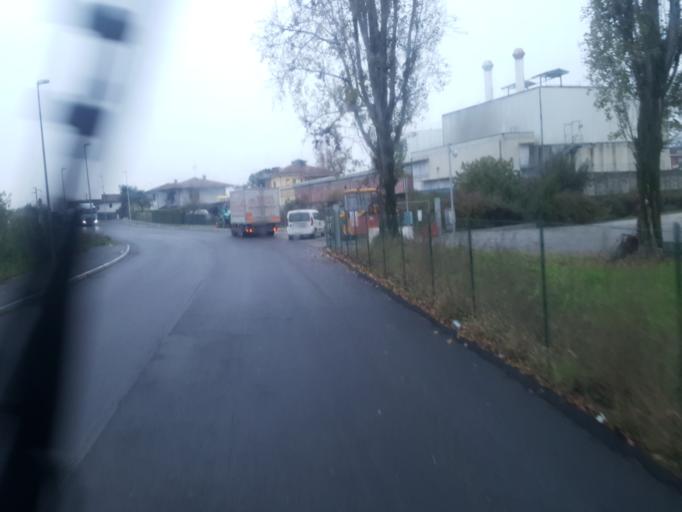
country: IT
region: Piedmont
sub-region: Provincia di Cuneo
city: Saluzzo
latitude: 44.6409
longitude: 7.5073
